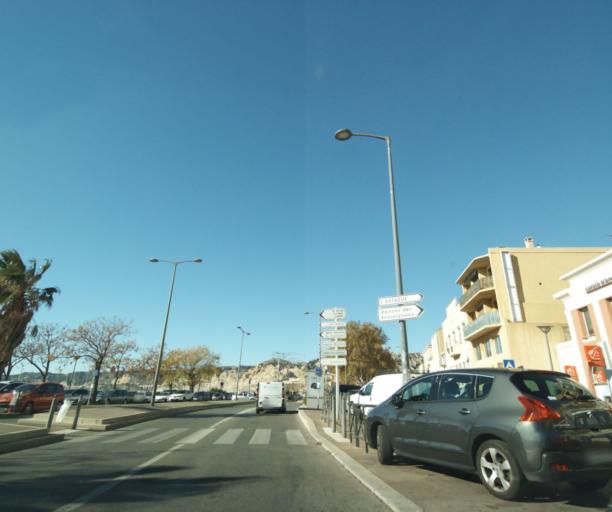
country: FR
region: Provence-Alpes-Cote d'Azur
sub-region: Departement des Bouches-du-Rhone
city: Marseille 16
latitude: 43.3598
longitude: 5.3161
